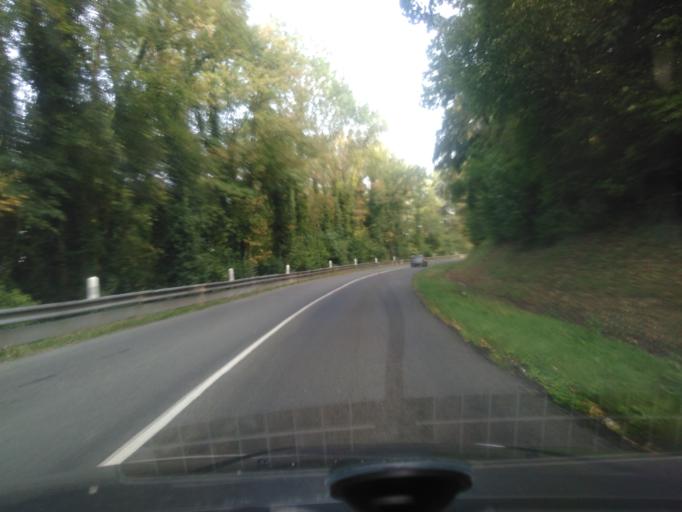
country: FR
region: Picardie
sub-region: Departement de l'Aisne
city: Bruyeres-et-Montberault
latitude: 49.5135
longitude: 3.6745
